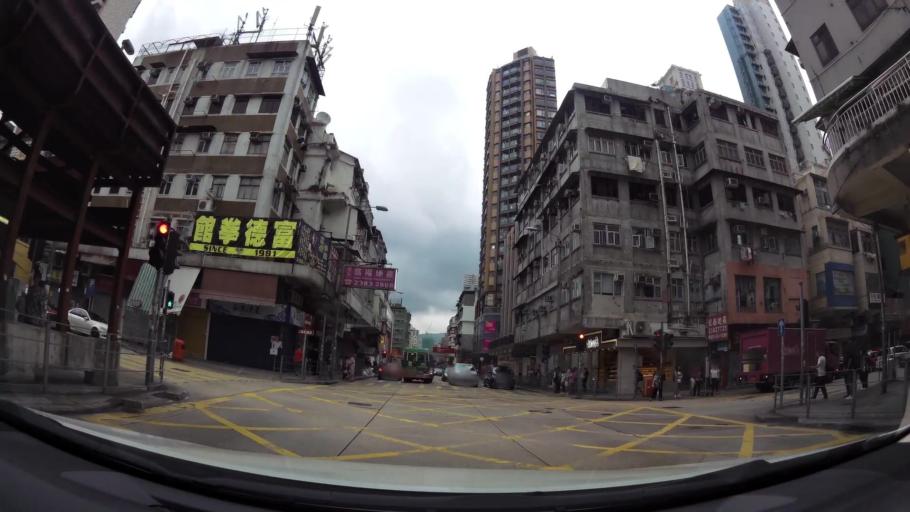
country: HK
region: Kowloon City
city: Kowloon
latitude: 22.3289
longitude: 114.1882
